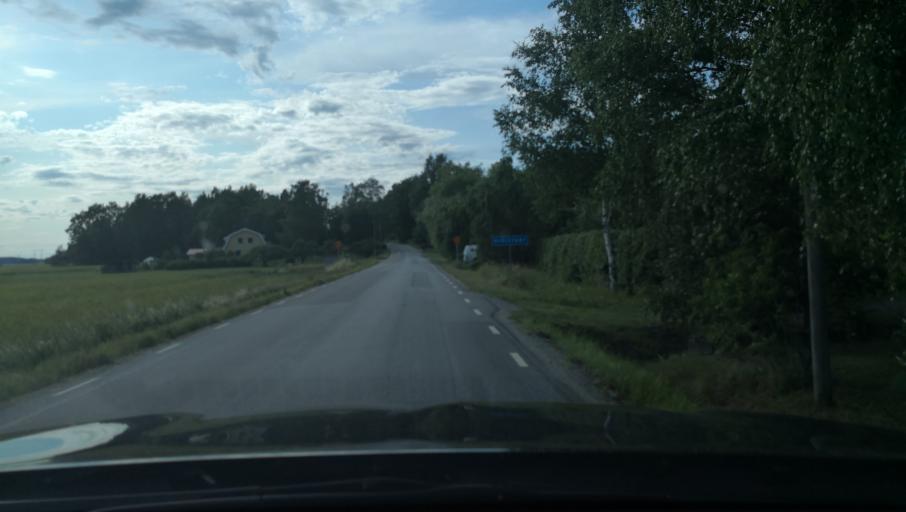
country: SE
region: Uppsala
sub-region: Enkopings Kommun
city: Orsundsbro
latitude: 59.6872
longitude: 17.3898
